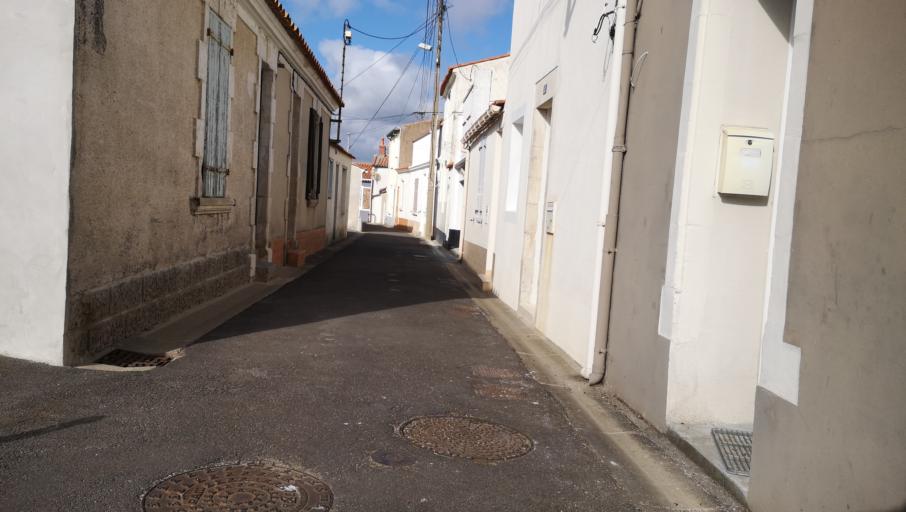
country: FR
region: Pays de la Loire
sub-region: Departement de la Vendee
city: Les Sables-d'Olonne
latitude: 46.4980
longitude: -1.7999
